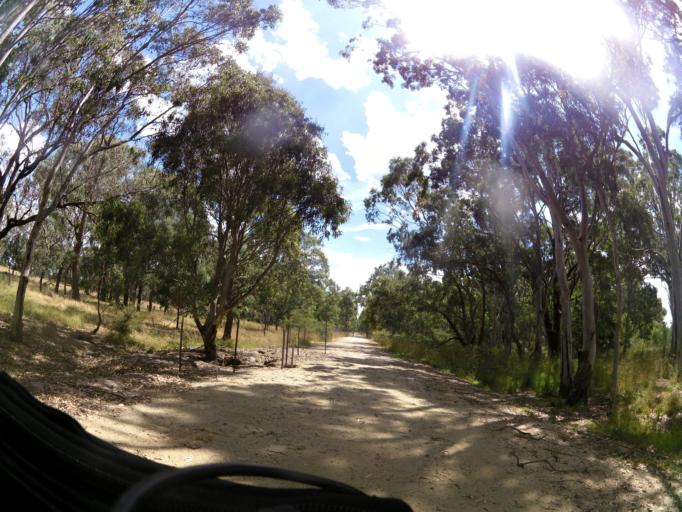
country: AU
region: Victoria
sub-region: Wellington
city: Heyfield
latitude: -37.9826
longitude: 146.7296
